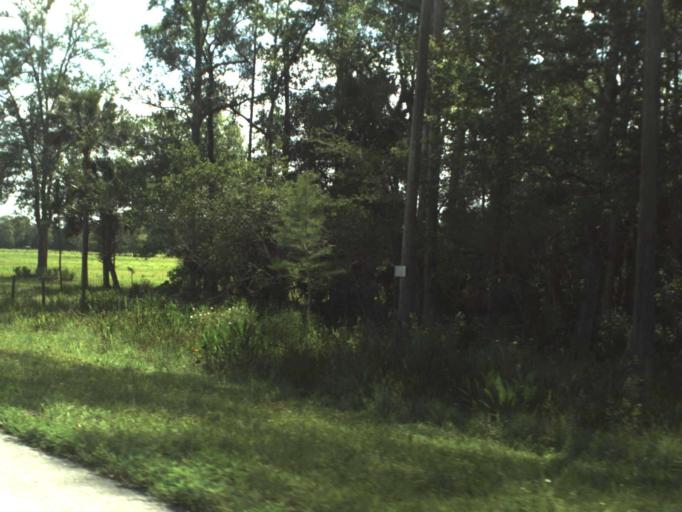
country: US
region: Florida
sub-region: Volusia County
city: Lake Helen
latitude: 28.9207
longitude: -81.1182
